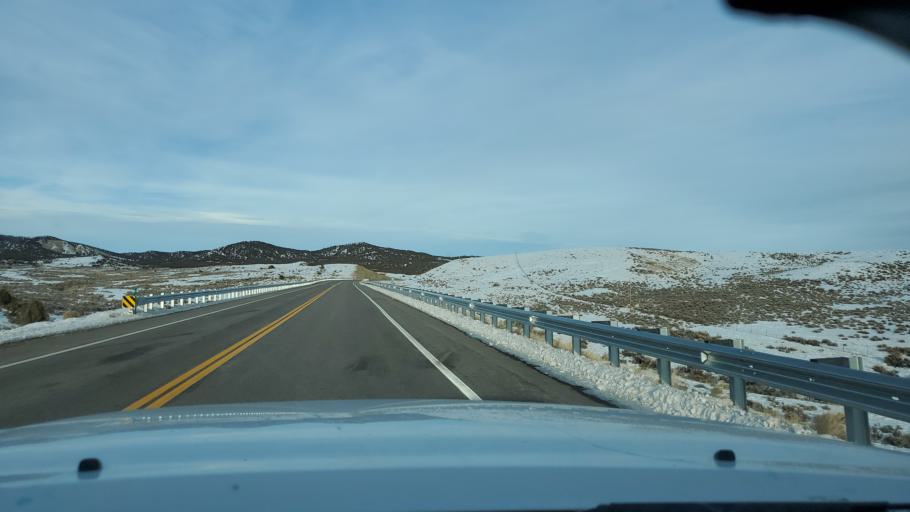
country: US
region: Colorado
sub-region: Rio Blanco County
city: Rangely
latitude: 40.3301
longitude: -108.4918
